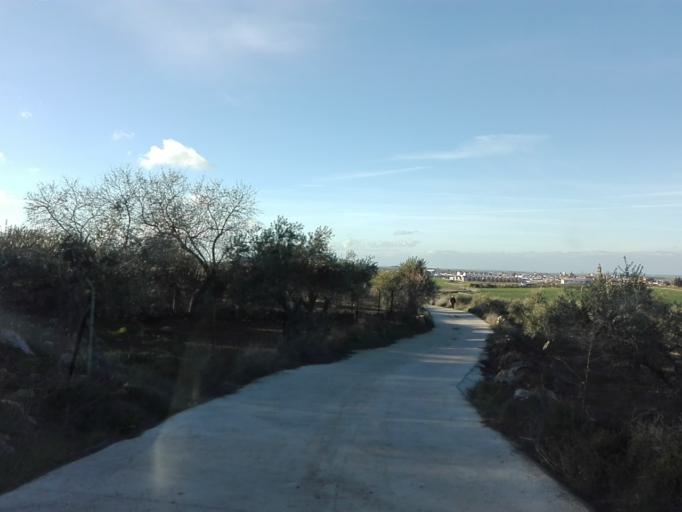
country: ES
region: Extremadura
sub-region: Provincia de Badajoz
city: Llerena
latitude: 38.2235
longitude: -6.0073
